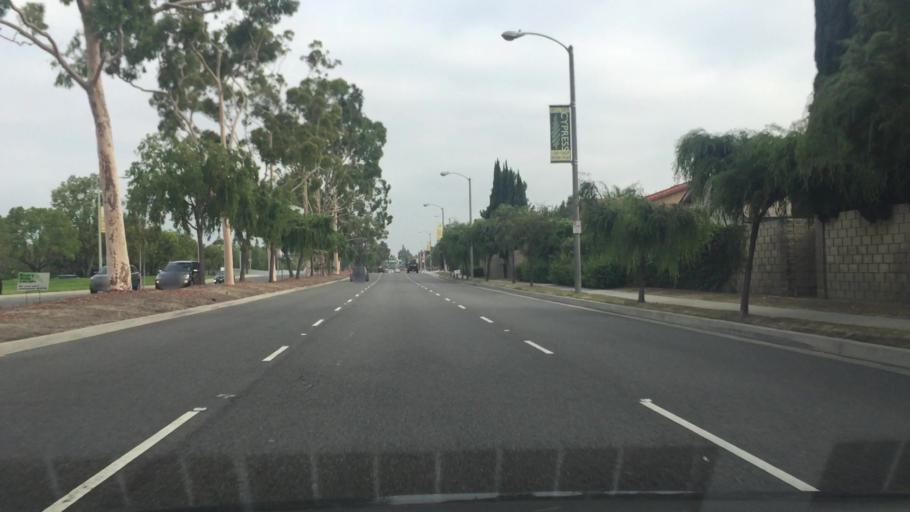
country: US
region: California
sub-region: Orange County
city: Cypress
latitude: 33.7980
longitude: -118.0283
